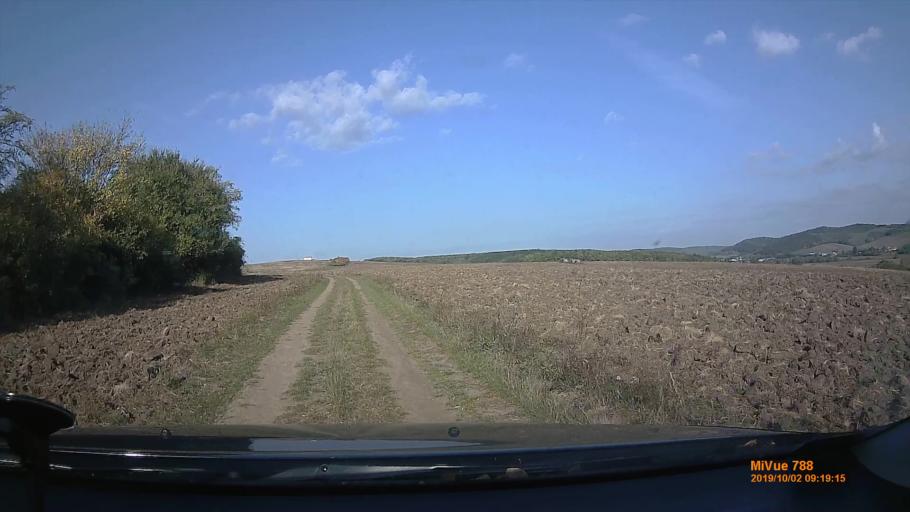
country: HU
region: Nograd
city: Kazar
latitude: 48.0229
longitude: 19.8155
